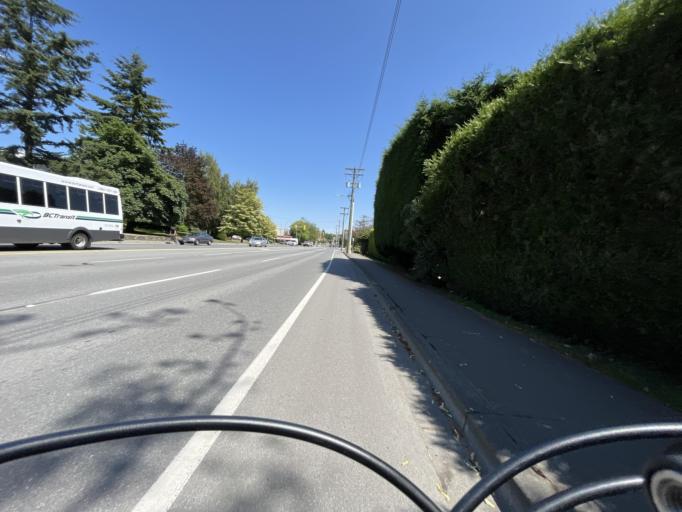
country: CA
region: British Columbia
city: Oak Bay
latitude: 48.4686
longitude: -123.3370
